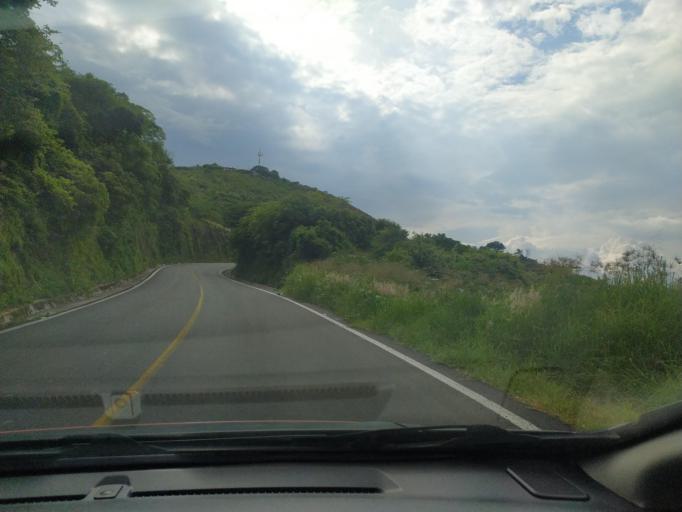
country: MX
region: Jalisco
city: Villa Corona
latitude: 20.3936
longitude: -103.6758
